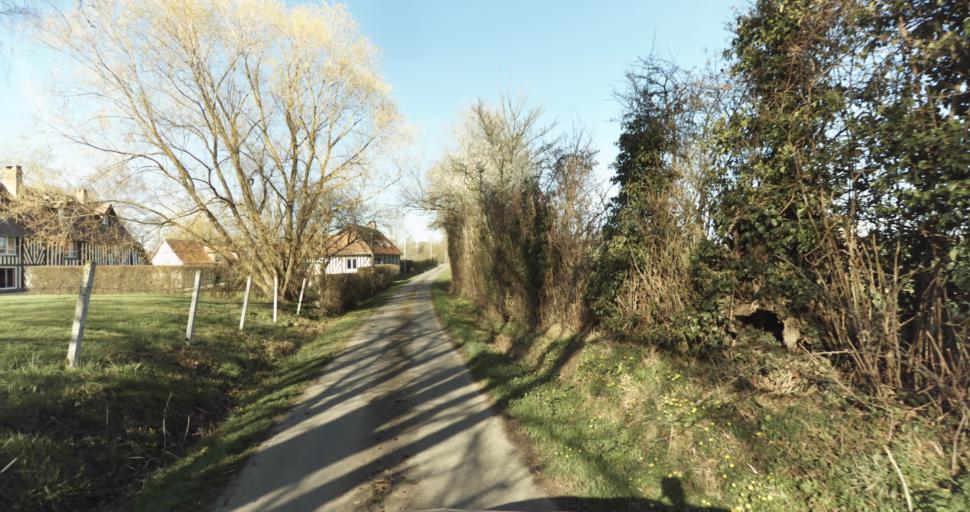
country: FR
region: Lower Normandy
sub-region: Departement du Calvados
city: Livarot
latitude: 49.0534
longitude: 0.0726
